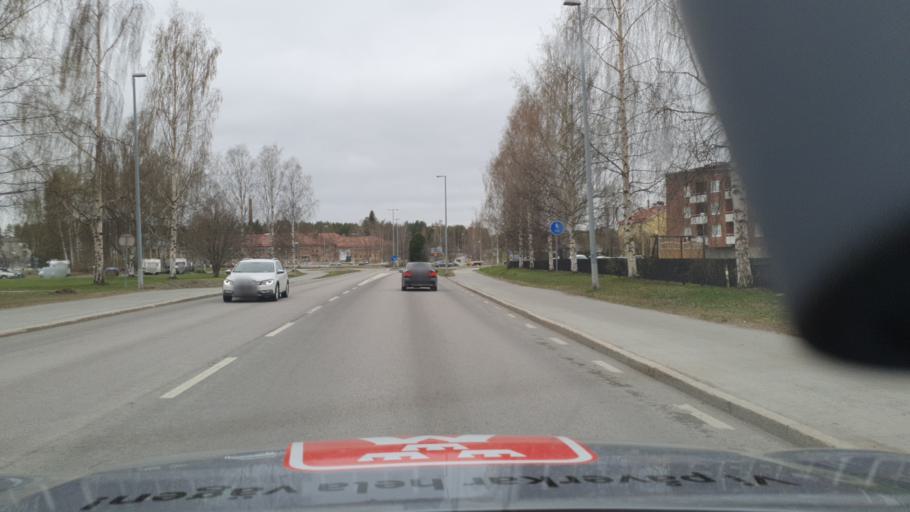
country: SE
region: Norrbotten
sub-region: Bodens Kommun
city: Boden
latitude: 65.8228
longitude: 21.6724
